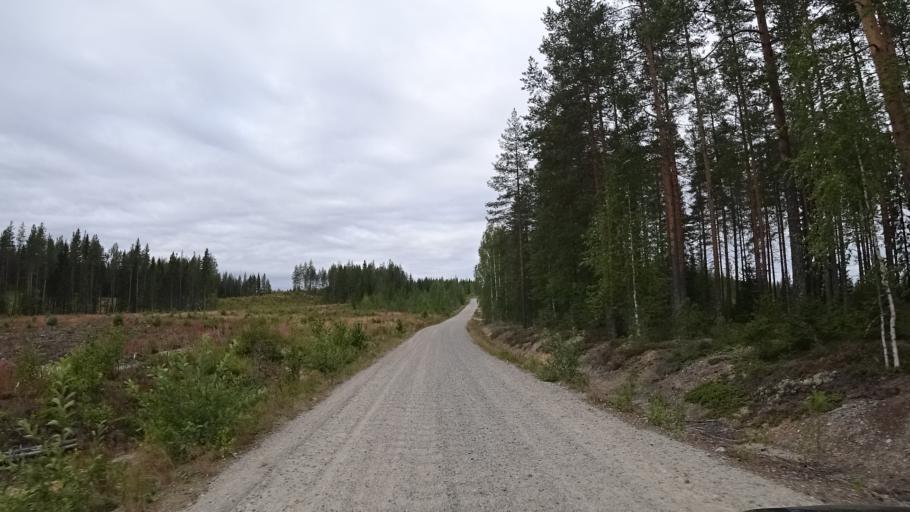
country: FI
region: North Karelia
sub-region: Joensuu
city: Ilomantsi
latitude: 63.1552
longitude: 30.6328
